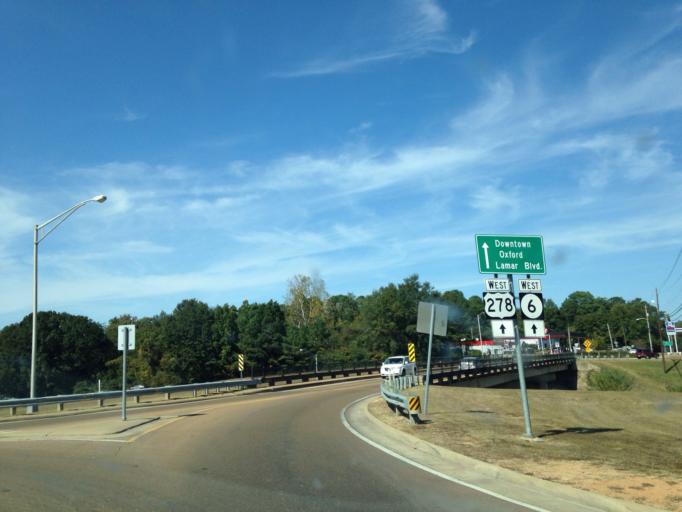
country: US
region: Mississippi
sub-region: Lafayette County
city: Oxford
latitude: 34.3537
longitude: -89.5211
